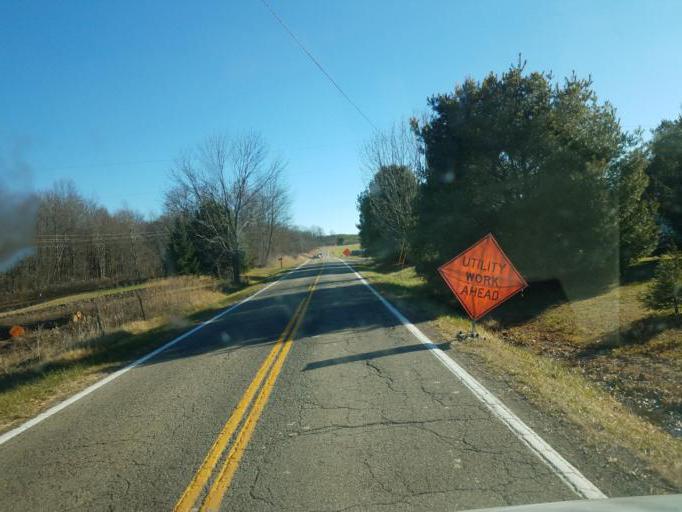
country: US
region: Ohio
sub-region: Knox County
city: Oak Hill
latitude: 40.2885
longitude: -82.1545
